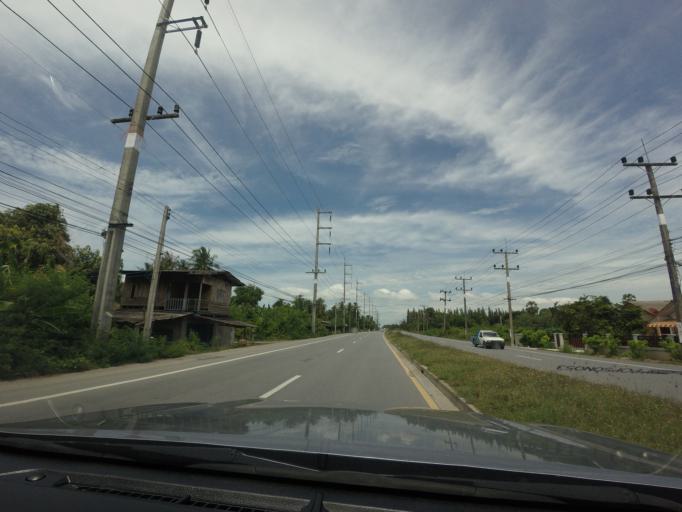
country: TH
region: Songkhla
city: Ranot
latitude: 7.7096
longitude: 100.3726
